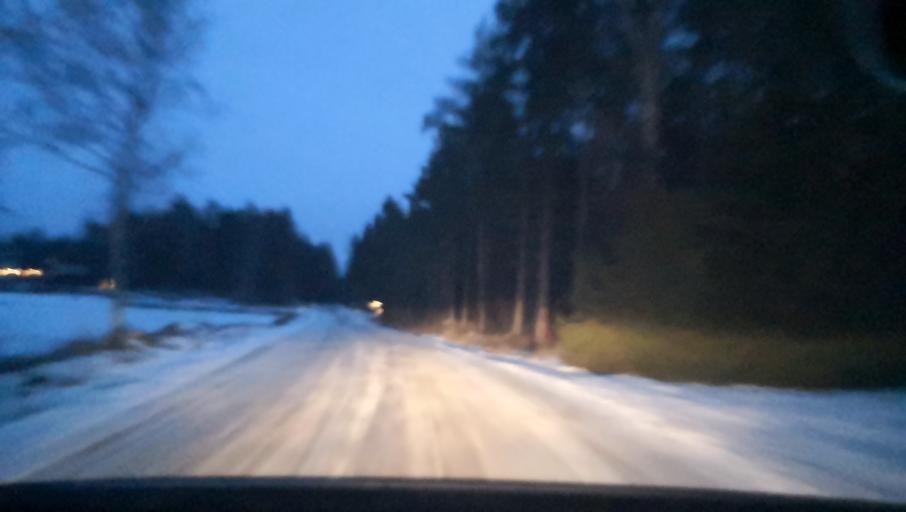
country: SE
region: Uppsala
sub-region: Heby Kommun
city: Tarnsjo
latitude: 60.2411
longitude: 16.7013
